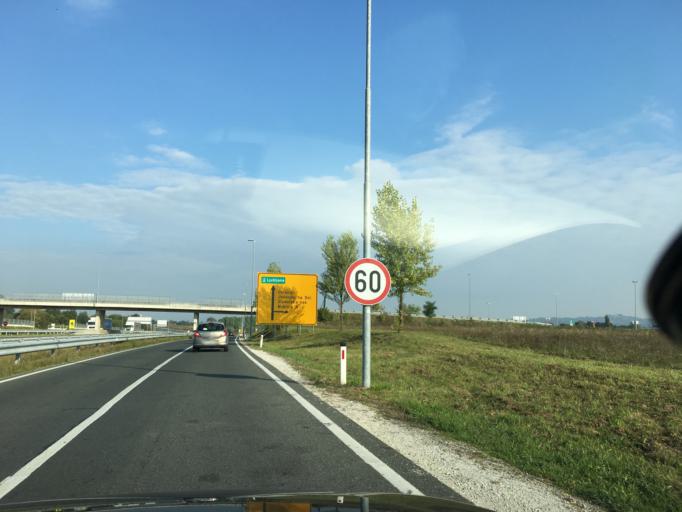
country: HR
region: Zagrebacka
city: Bregana
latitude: 45.8552
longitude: 15.6855
